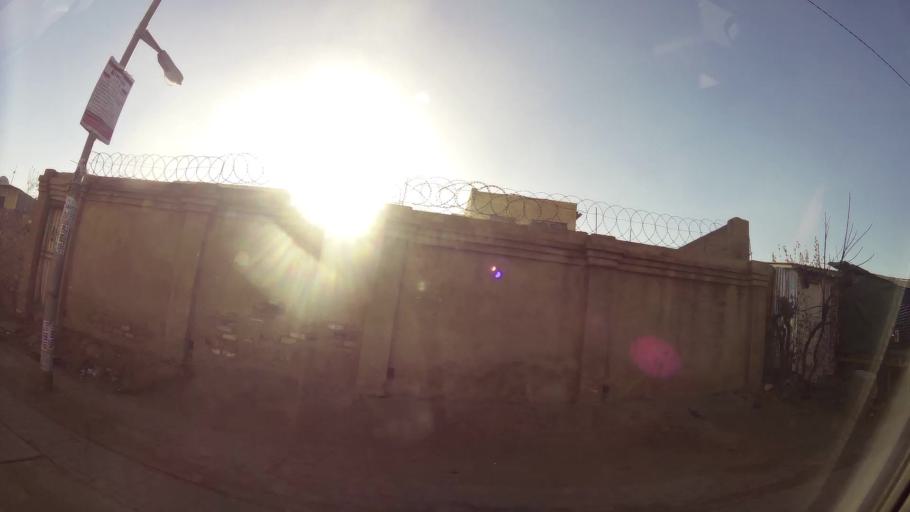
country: ZA
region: Gauteng
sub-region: City of Johannesburg Metropolitan Municipality
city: Diepsloot
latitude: -25.9262
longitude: 28.0080
